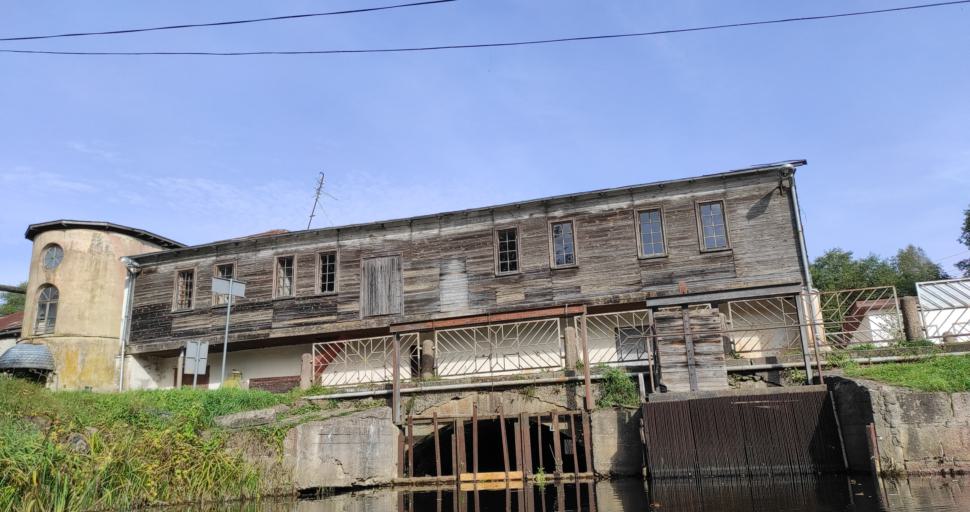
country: LV
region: Kuldigas Rajons
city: Kuldiga
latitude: 57.2430
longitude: 22.0849
